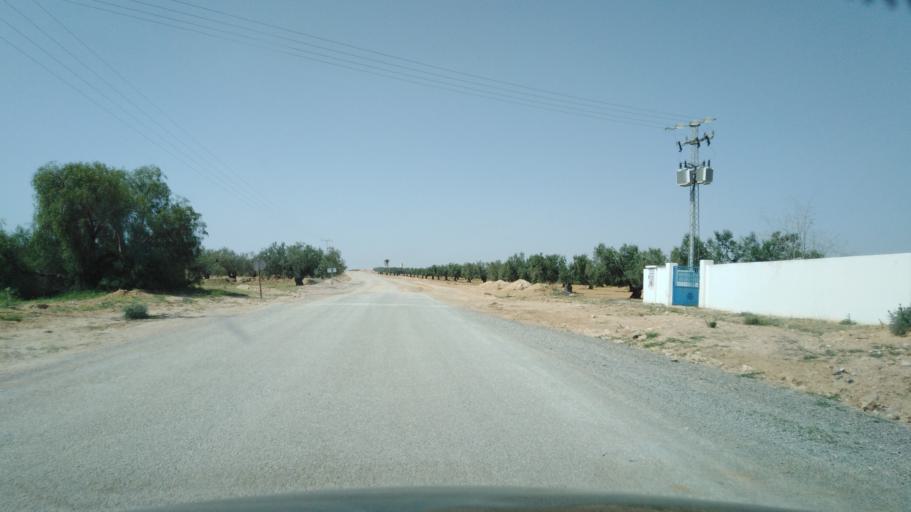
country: TN
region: Safaqis
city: Sfax
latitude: 34.6871
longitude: 10.4636
